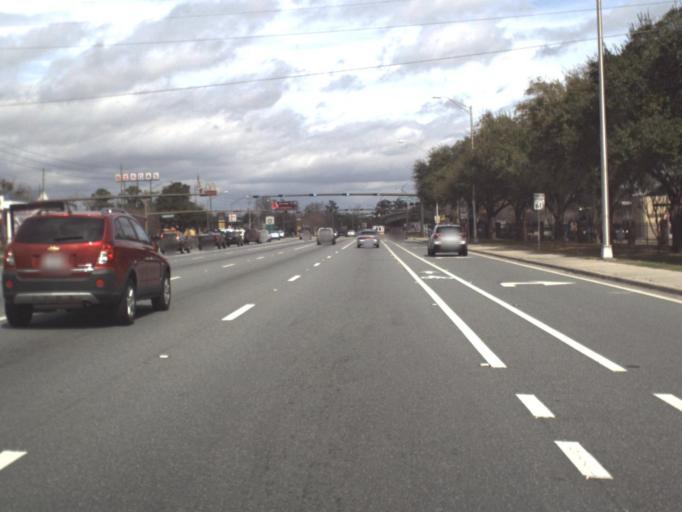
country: US
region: Florida
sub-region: Leon County
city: Tallahassee
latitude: 30.5032
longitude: -84.2513
